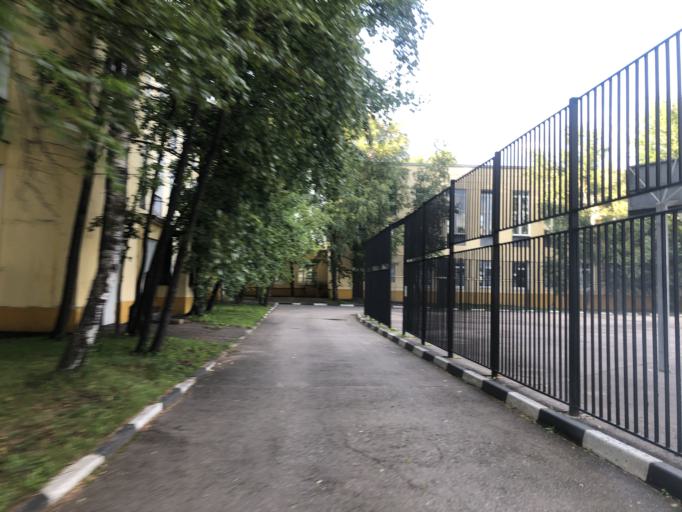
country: RU
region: Moskovskaya
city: Bol'shaya Setun'
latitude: 55.7369
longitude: 37.3950
